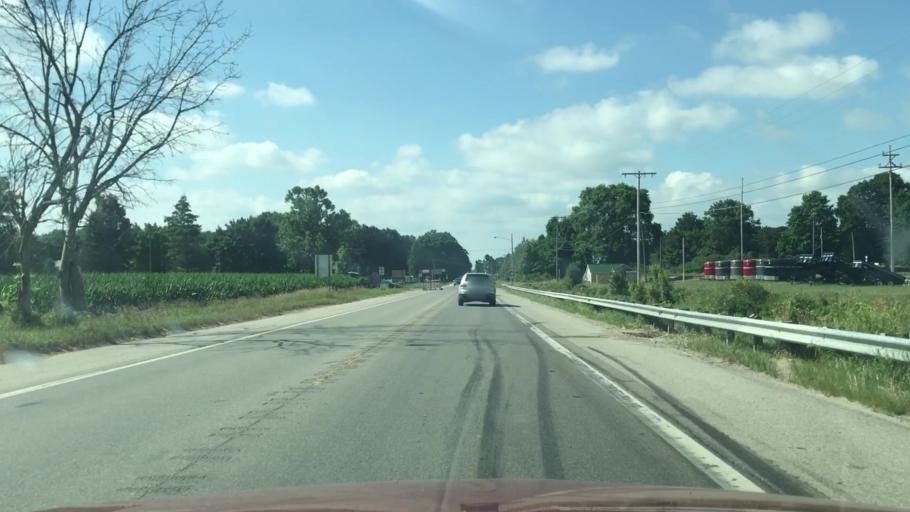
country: US
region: Michigan
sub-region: Newaygo County
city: Newaygo
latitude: 43.3233
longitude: -85.8106
